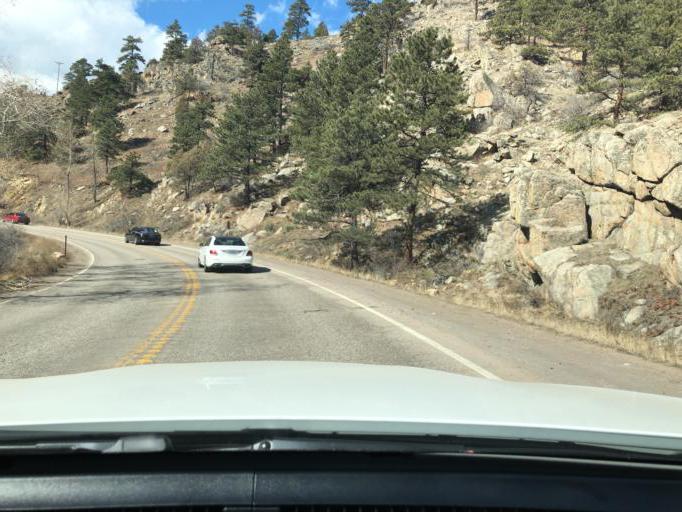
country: US
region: Colorado
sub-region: Boulder County
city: Boulder
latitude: 40.0050
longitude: -105.3600
